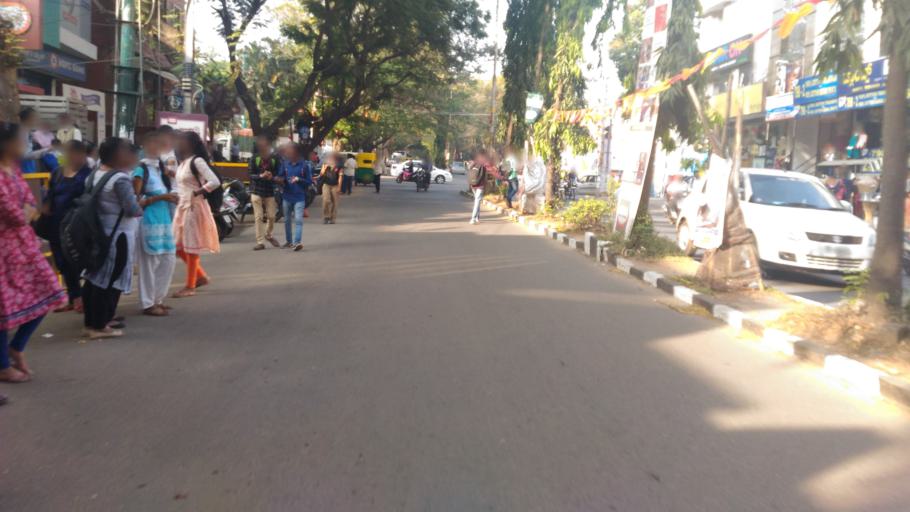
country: IN
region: Karnataka
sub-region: Bangalore Urban
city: Bangalore
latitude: 12.9227
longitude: 77.5934
